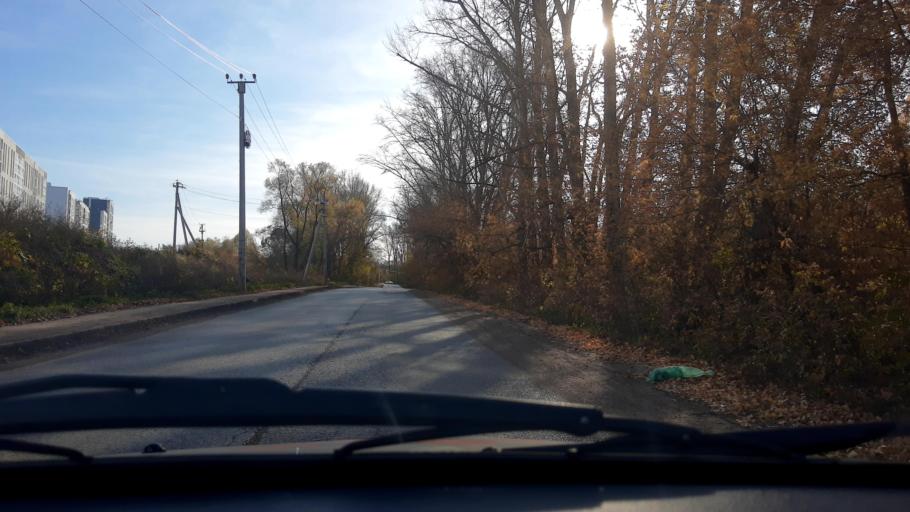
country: RU
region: Bashkortostan
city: Ufa
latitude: 54.6948
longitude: 55.9678
